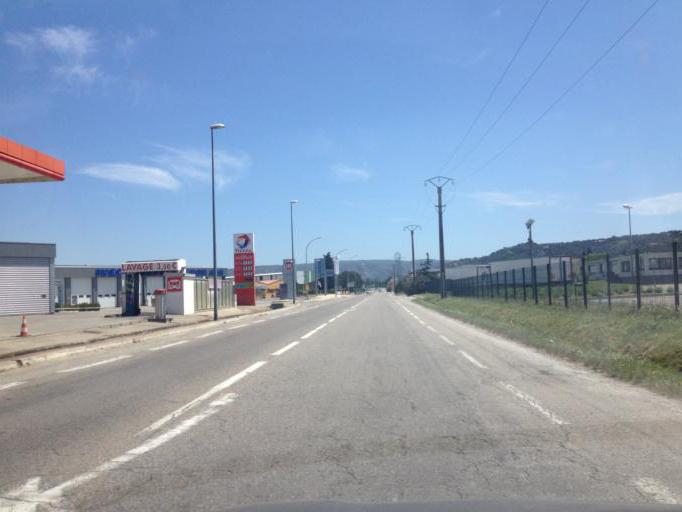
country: FR
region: Provence-Alpes-Cote d'Azur
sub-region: Departement du Vaucluse
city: Cavaillon
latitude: 43.8568
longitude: 5.0168
